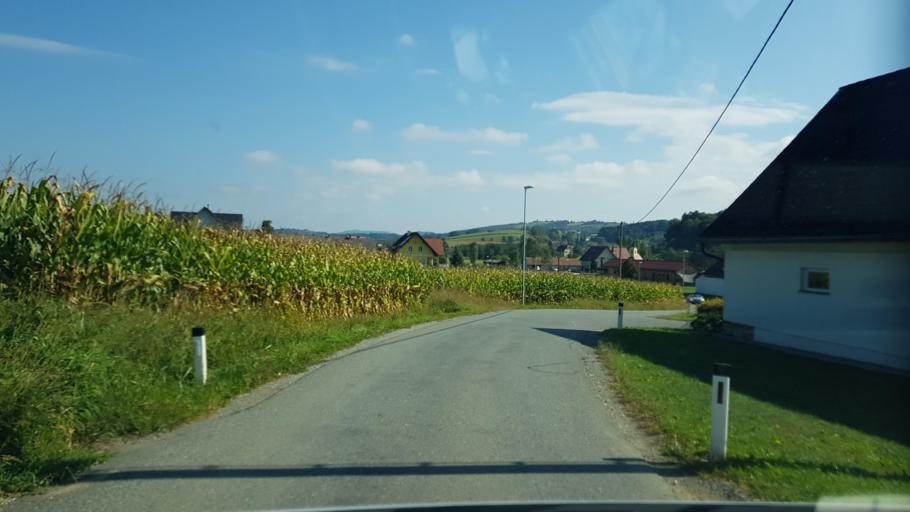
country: AT
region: Styria
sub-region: Politischer Bezirk Deutschlandsberg
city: Wettmannstatten
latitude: 46.8117
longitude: 15.3863
